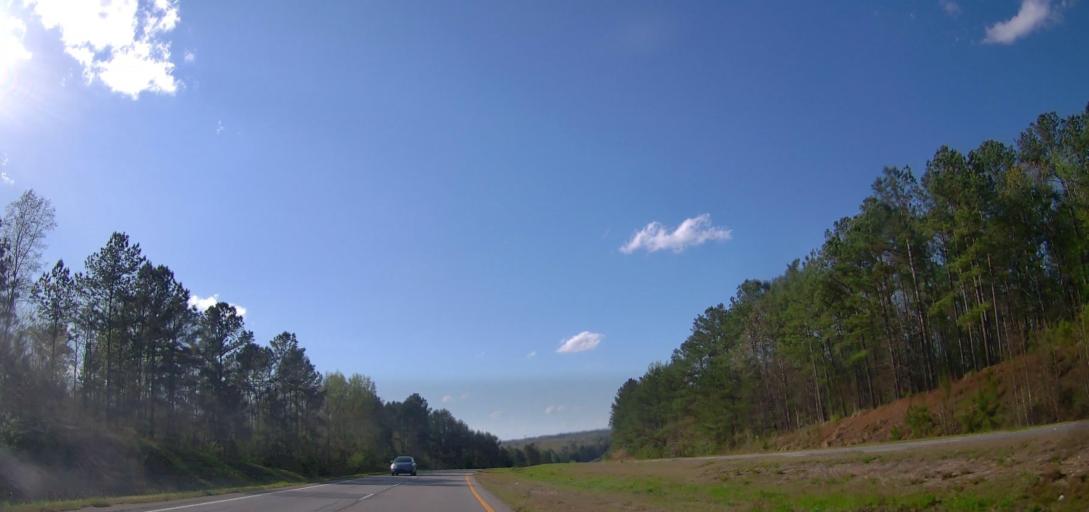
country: US
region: Georgia
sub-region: Baldwin County
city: Hardwick
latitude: 33.0275
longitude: -83.2443
